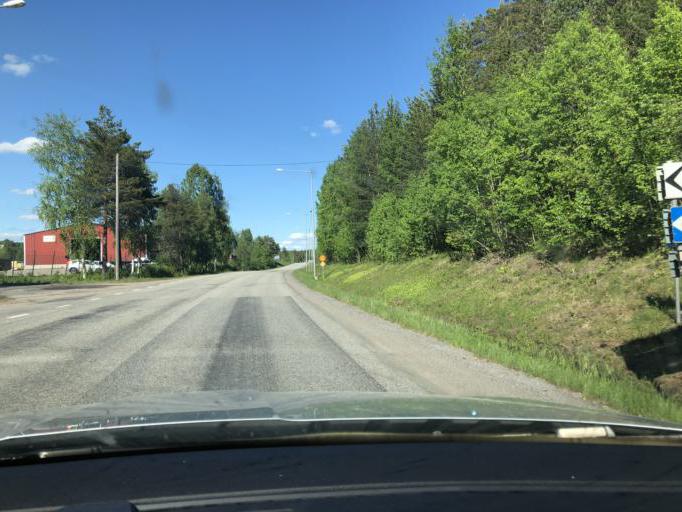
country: SE
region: Norrbotten
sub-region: Kalix Kommun
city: Kalix
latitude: 65.8671
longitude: 23.1420
